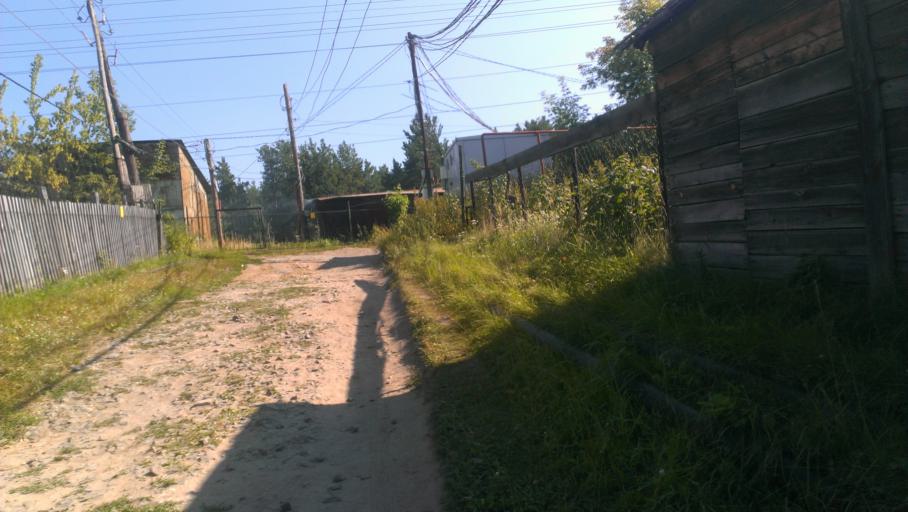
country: RU
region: Altai Krai
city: Novosilikatnyy
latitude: 53.3204
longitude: 83.6849
